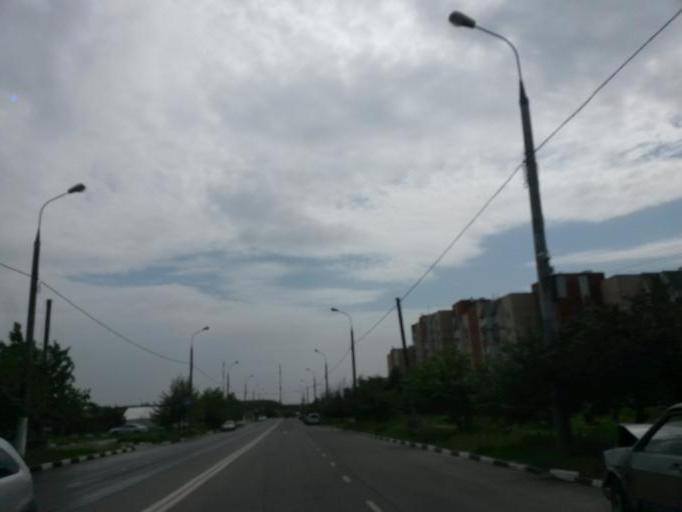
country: RU
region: Moskovskaya
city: Shcherbinka
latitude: 55.5367
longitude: 37.5351
